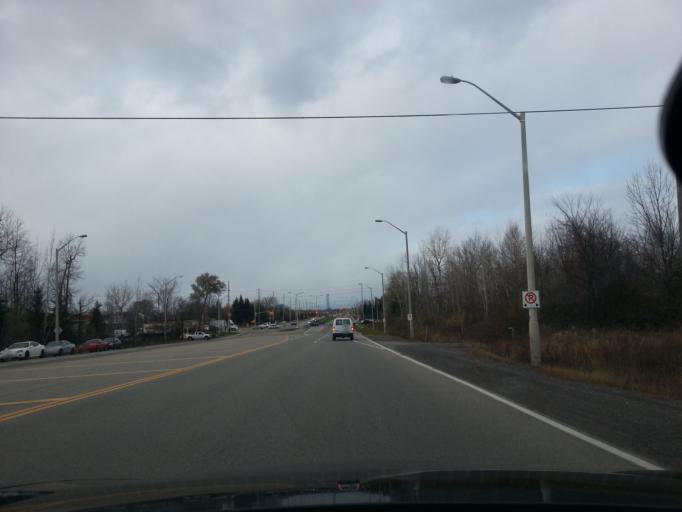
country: CA
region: Ontario
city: Ottawa
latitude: 45.3633
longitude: -75.6184
